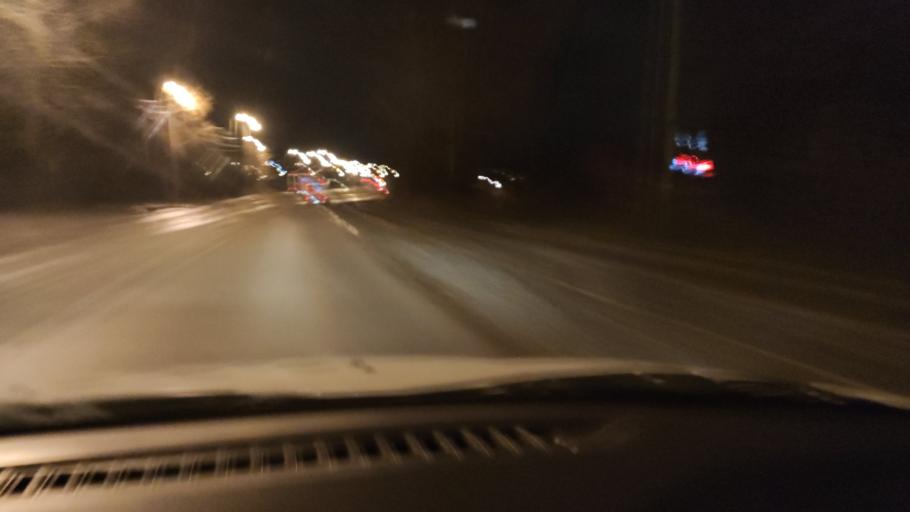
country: RU
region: Perm
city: Kondratovo
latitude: 57.9558
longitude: 56.1349
